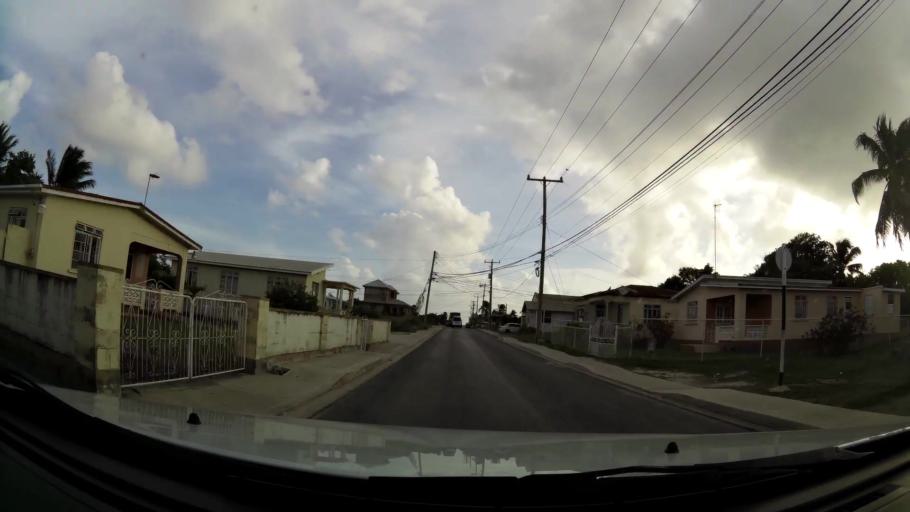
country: BB
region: Christ Church
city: Oistins
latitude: 13.0536
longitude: -59.5192
